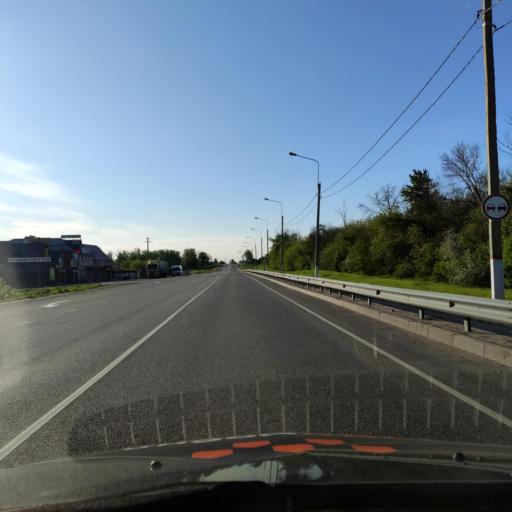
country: RU
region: Lipetsk
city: Yelets
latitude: 52.5578
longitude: 38.6951
